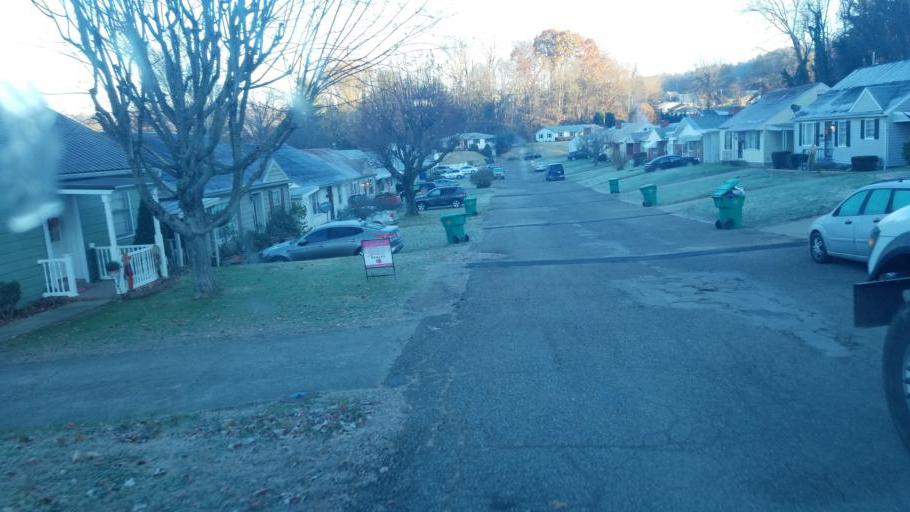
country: US
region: Ohio
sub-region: Scioto County
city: Portsmouth
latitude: 38.7483
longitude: -82.9728
